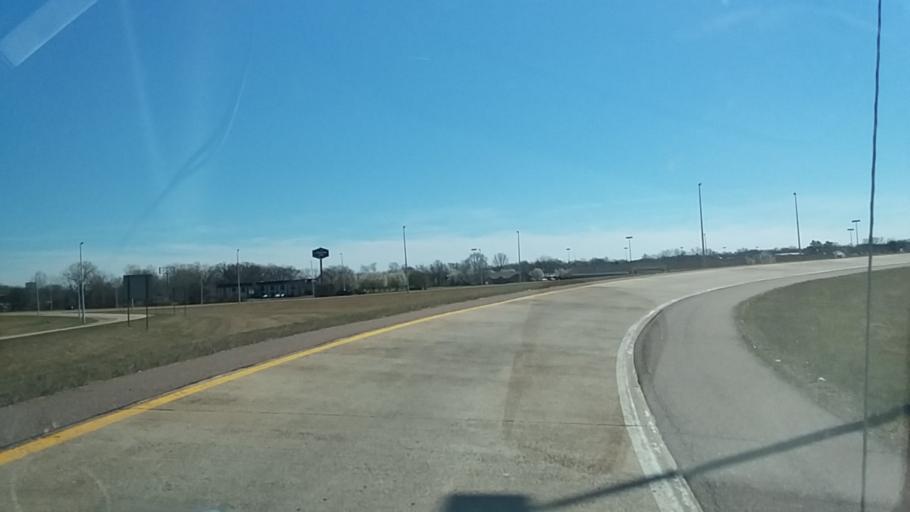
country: US
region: Tennessee
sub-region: Dyer County
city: Dyersburg
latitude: 36.0700
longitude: -89.3951
